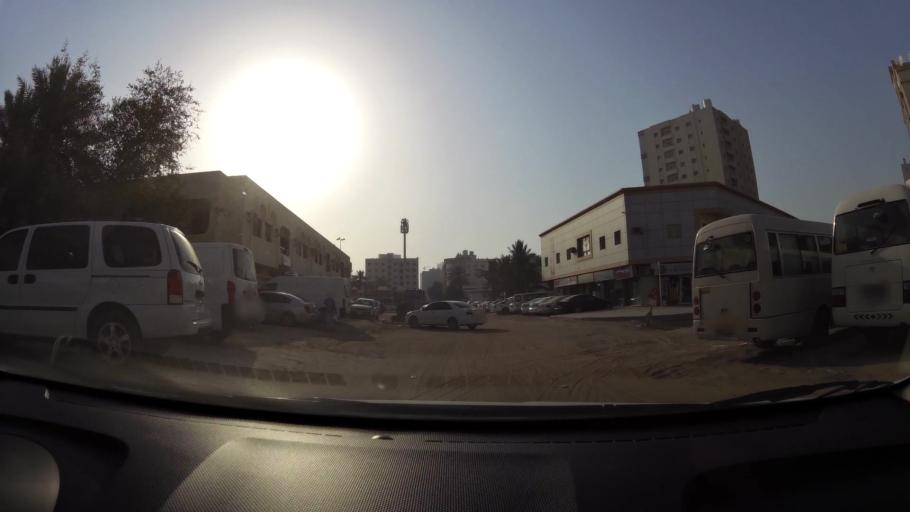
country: AE
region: Ajman
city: Ajman
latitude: 25.3836
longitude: 55.4458
